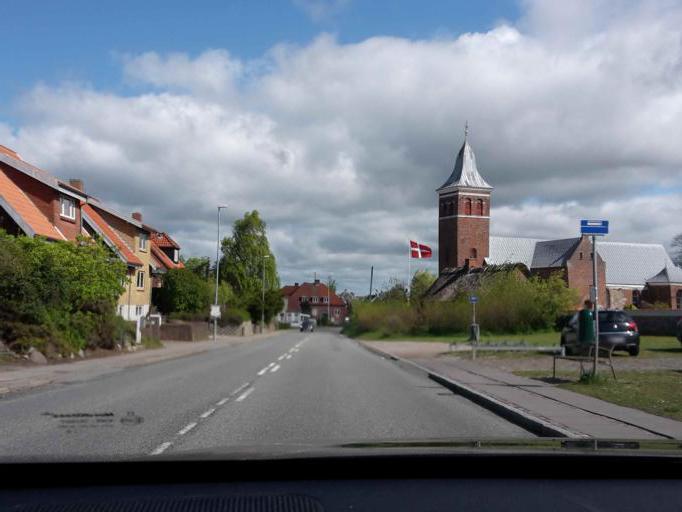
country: DK
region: Central Jutland
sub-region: Syddjurs Kommune
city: Hornslet
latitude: 56.3131
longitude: 10.3201
